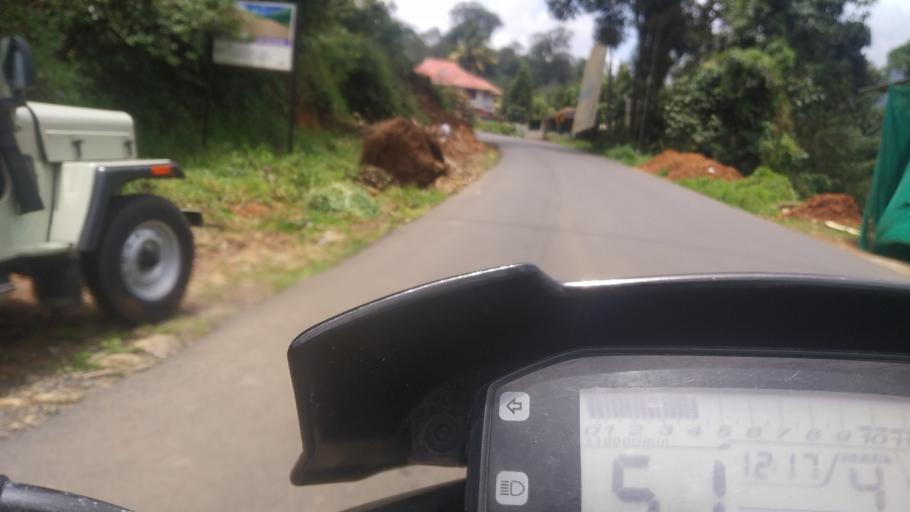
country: IN
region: Kerala
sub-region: Idukki
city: Munnar
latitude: 10.0182
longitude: 77.0120
